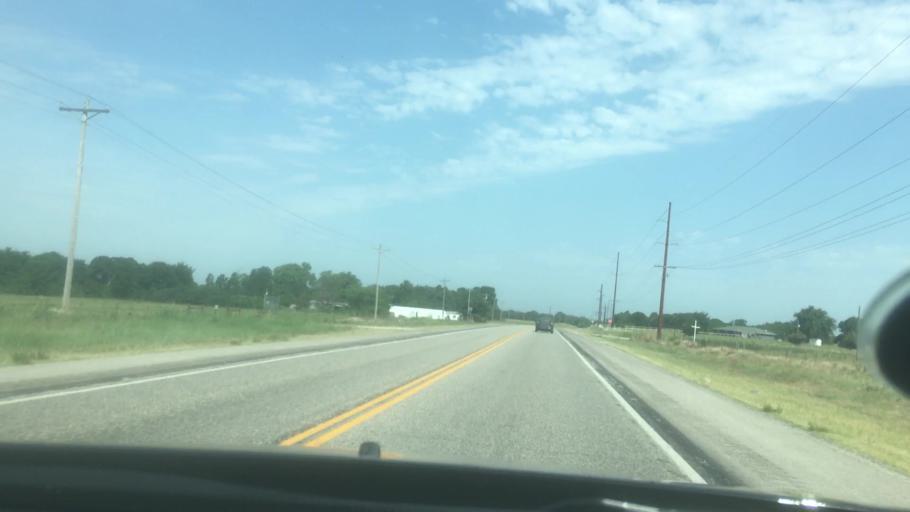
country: US
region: Oklahoma
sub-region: Seminole County
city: Konawa
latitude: 34.8533
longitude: -96.8146
